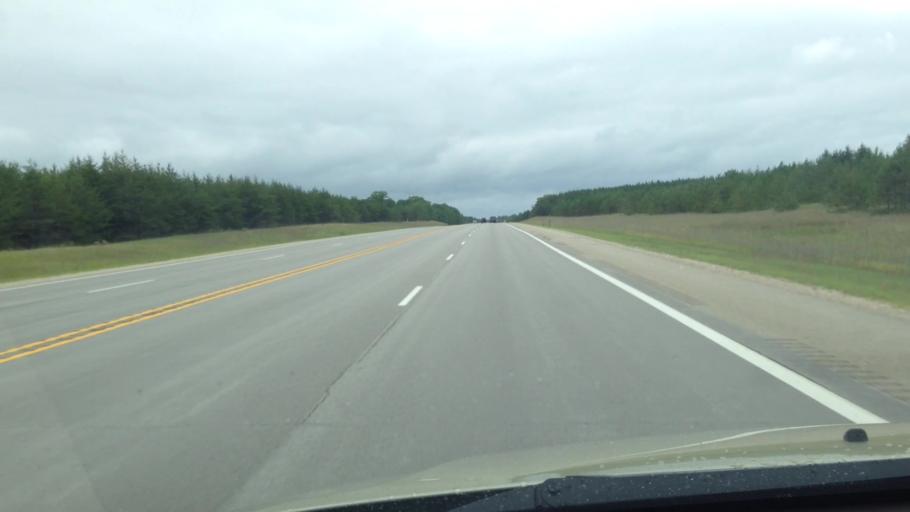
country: US
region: Michigan
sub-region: Schoolcraft County
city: Manistique
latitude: 45.9081
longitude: -86.4280
